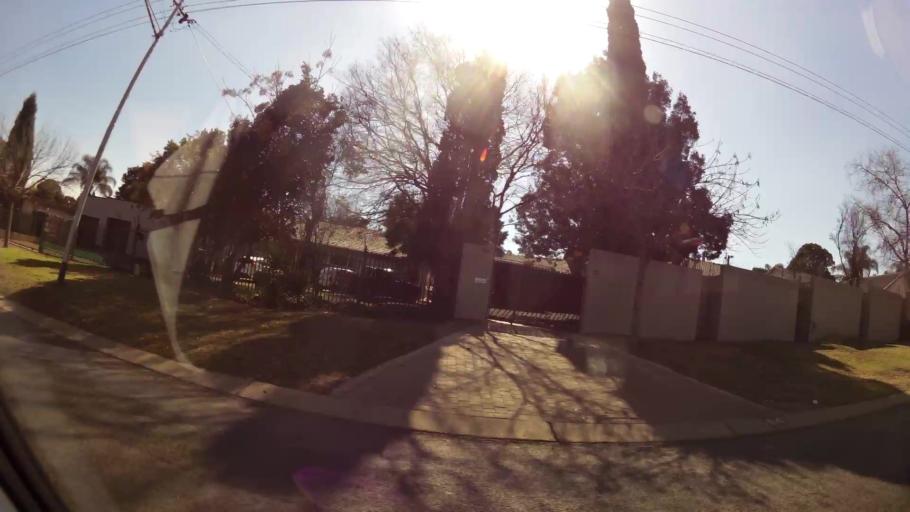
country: ZA
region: Gauteng
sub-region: City of Tshwane Metropolitan Municipality
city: Centurion
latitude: -25.8039
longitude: 28.2364
